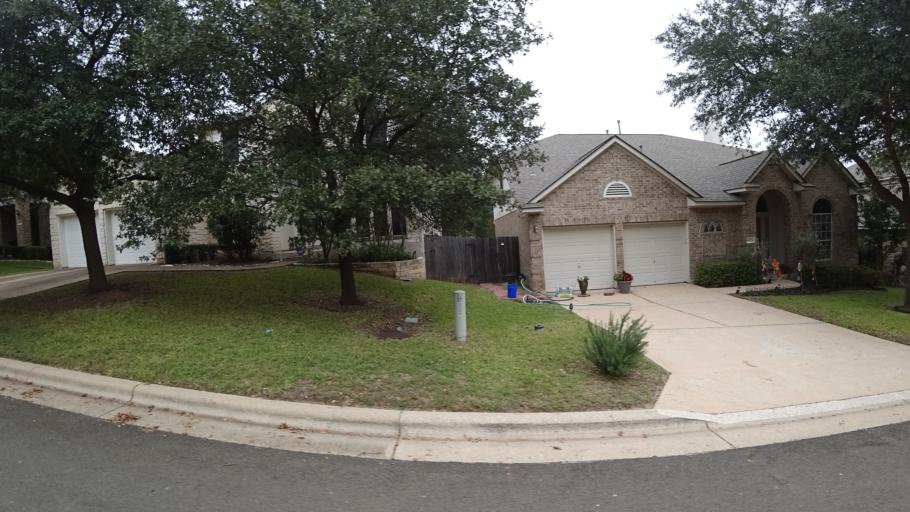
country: US
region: Texas
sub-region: Travis County
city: Shady Hollow
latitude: 30.2153
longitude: -97.8864
